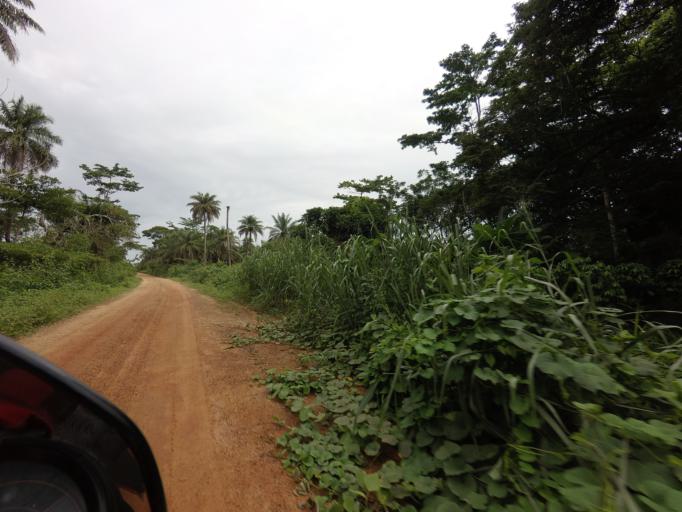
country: SL
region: Eastern Province
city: Jojoima
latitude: 7.9126
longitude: -10.7767
